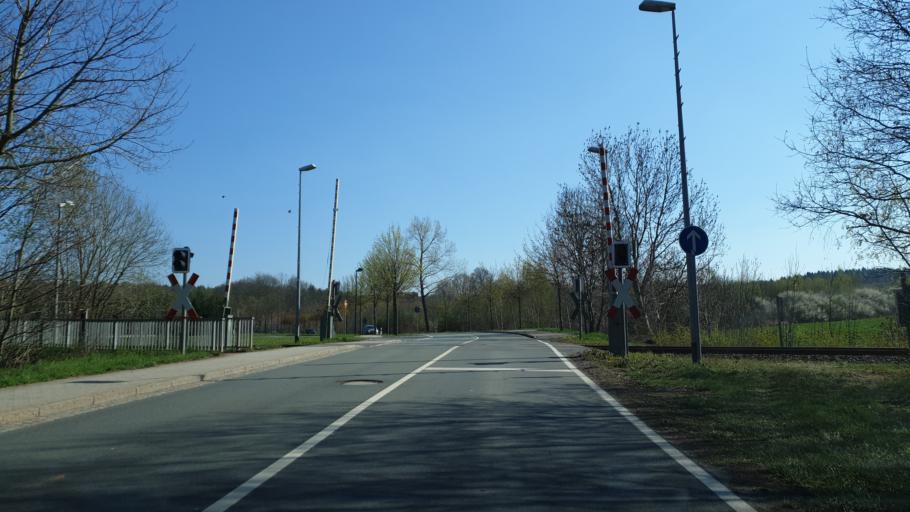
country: DE
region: Saxony
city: Oelsnitz
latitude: 50.7183
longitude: 12.7057
